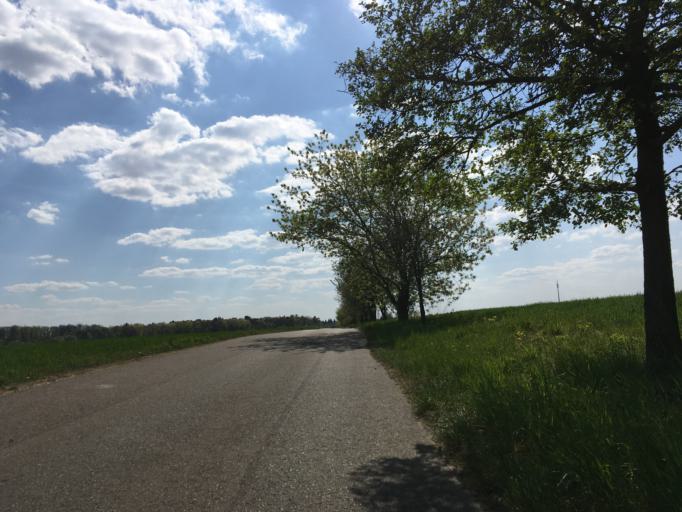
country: DE
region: Brandenburg
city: Ahrensfelde
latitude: 52.6026
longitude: 13.5934
